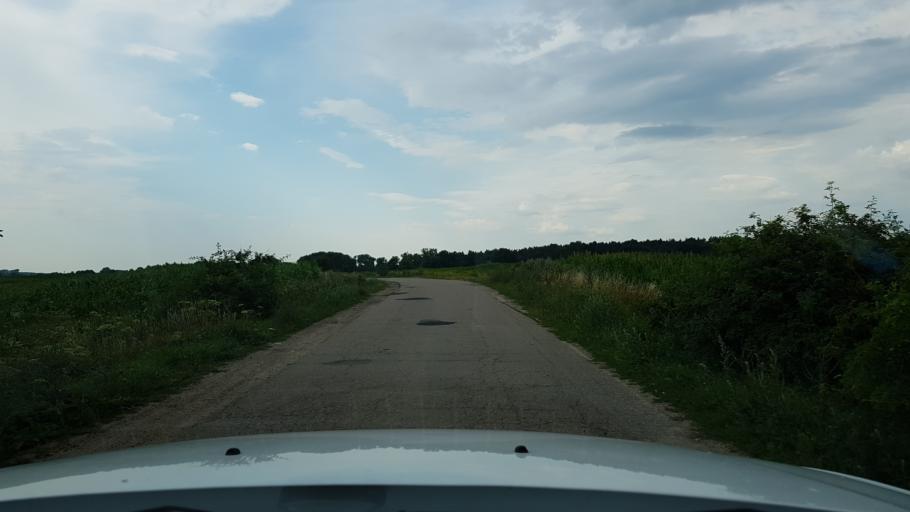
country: PL
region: West Pomeranian Voivodeship
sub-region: Powiat walecki
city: Walcz
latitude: 53.3622
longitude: 16.3443
